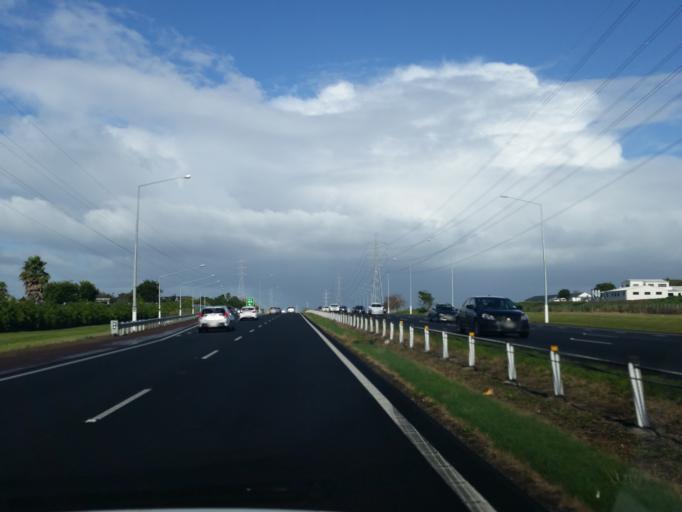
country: NZ
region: Auckland
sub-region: Auckland
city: Papakura
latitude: -37.0669
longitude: 174.9265
